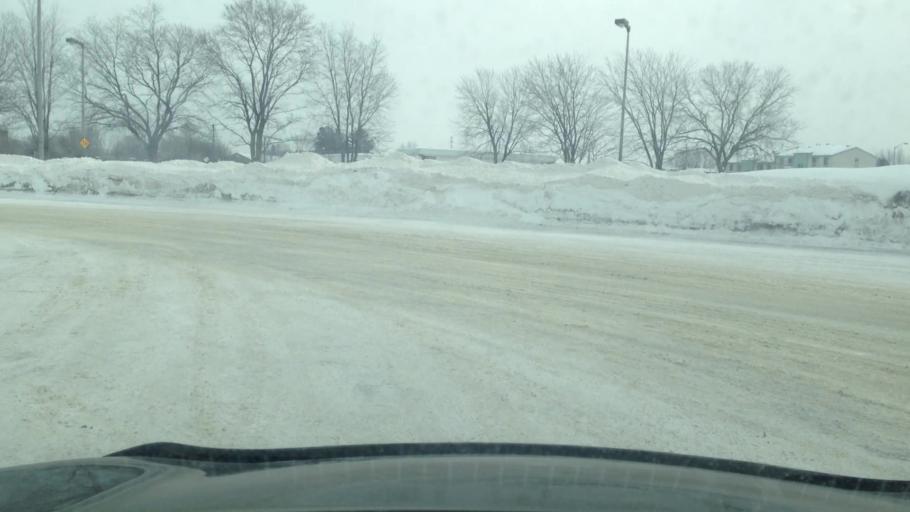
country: CA
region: Quebec
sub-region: Laurentides
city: Saint-Jerome
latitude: 45.7920
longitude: -74.0172
